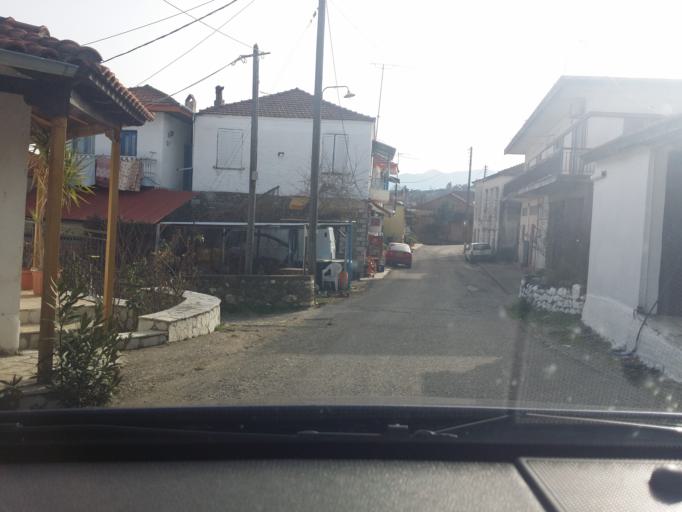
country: GR
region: West Greece
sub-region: Nomos Aitolias kai Akarnanias
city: Katouna
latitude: 38.8265
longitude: 21.0758
